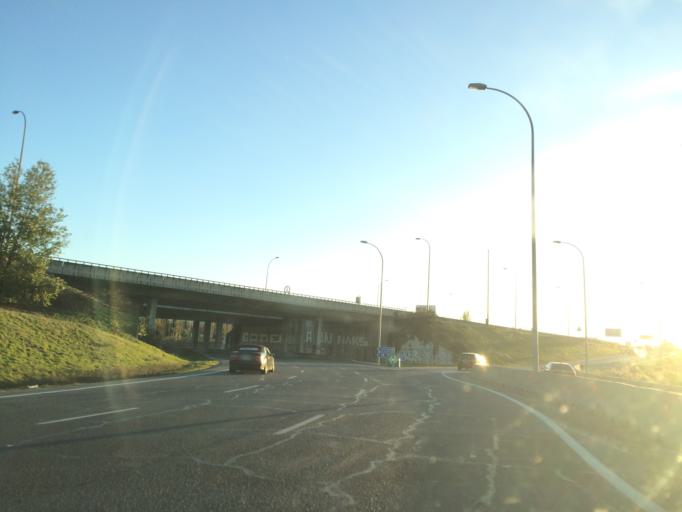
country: ES
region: Madrid
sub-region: Provincia de Madrid
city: Alcobendas
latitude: 40.5332
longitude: -3.6403
